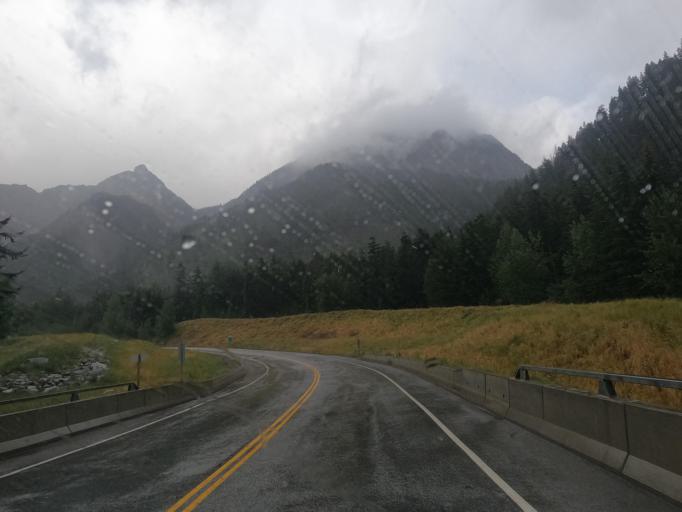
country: CA
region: British Columbia
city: Lillooet
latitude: 50.5339
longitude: -122.1506
